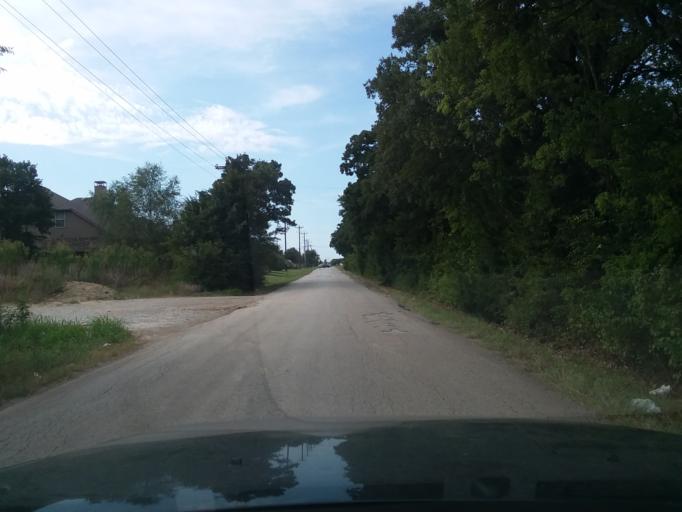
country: US
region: Texas
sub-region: Denton County
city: Bartonville
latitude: 33.1047
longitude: -97.1312
